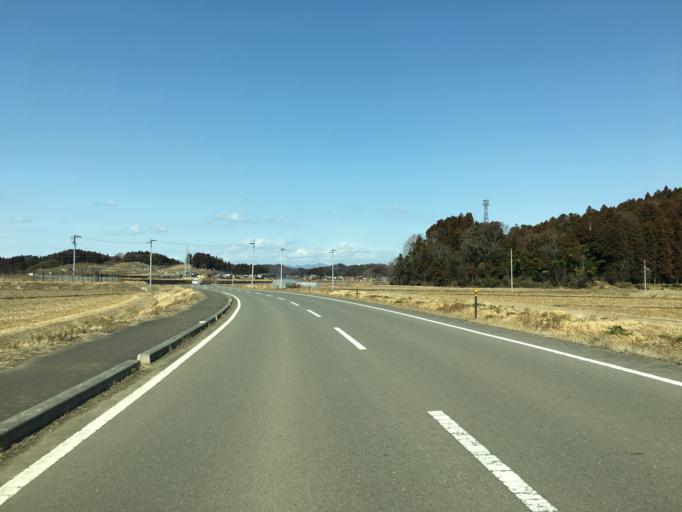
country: JP
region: Fukushima
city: Ishikawa
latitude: 37.1200
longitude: 140.2767
